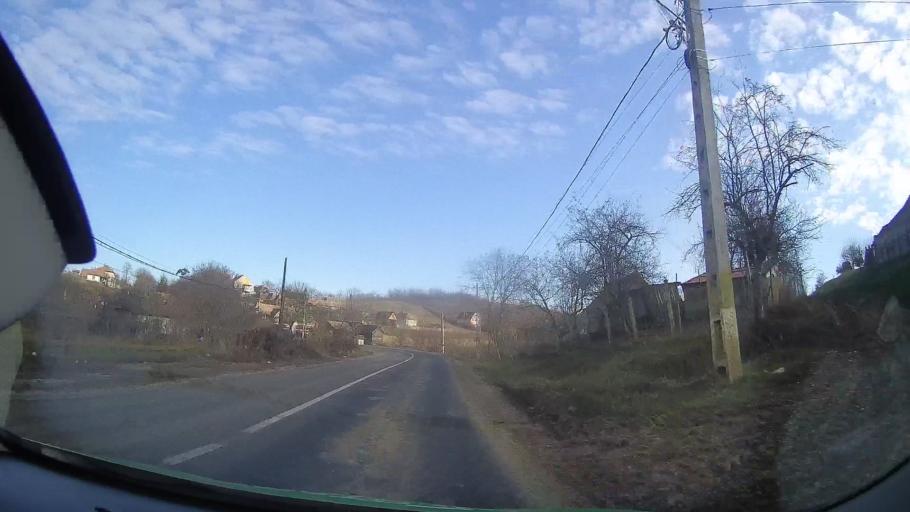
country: RO
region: Mures
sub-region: Comuna Iclanzel
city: Iclanzel
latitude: 46.5227
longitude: 24.2741
